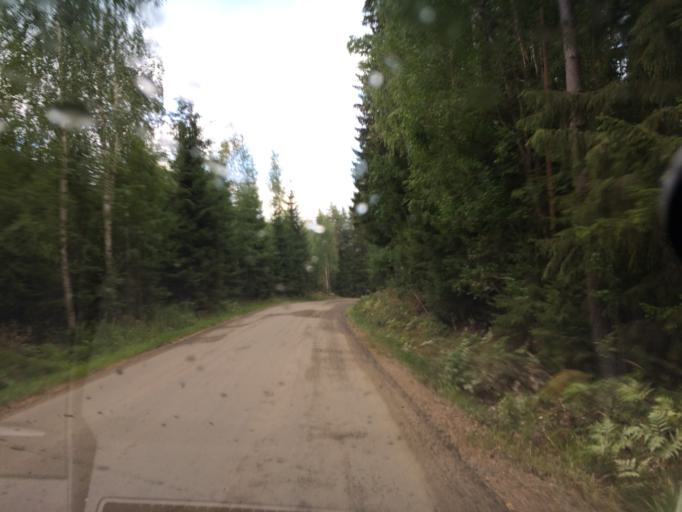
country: FI
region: Pirkanmaa
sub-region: Tampere
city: Luopioinen
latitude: 61.2695
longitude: 24.6786
